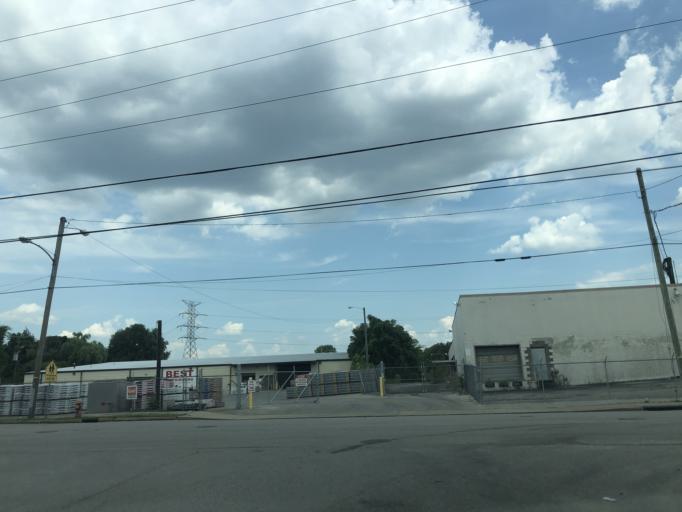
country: US
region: Tennessee
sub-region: Davidson County
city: Nashville
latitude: 36.1483
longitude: -86.7578
